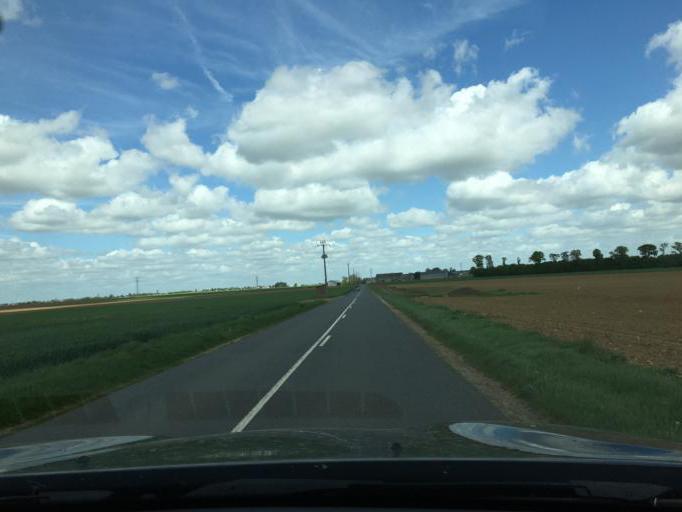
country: FR
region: Centre
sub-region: Departement du Loiret
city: Bricy
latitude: 48.0287
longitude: 1.8003
